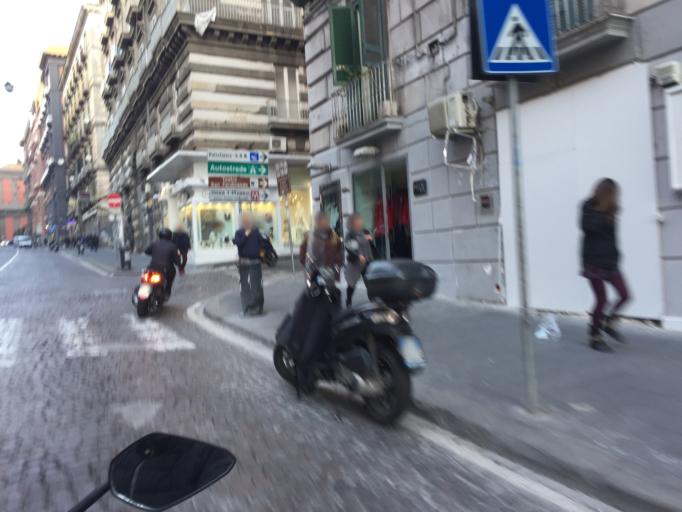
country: IT
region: Campania
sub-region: Provincia di Napoli
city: Napoli
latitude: 40.8508
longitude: 14.2501
